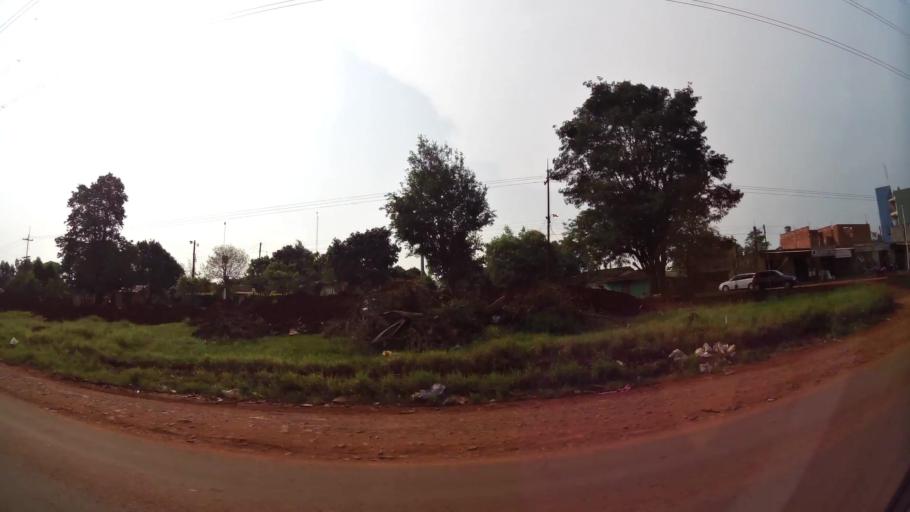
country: PY
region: Alto Parana
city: Ciudad del Este
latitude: -25.4764
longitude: -54.6523
